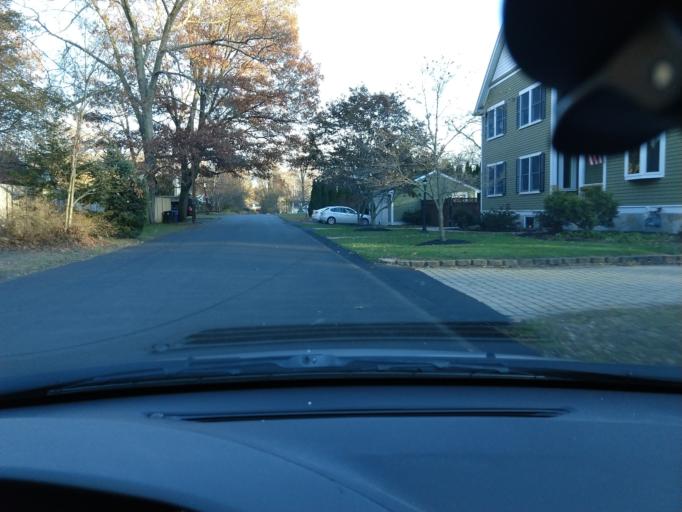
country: US
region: Massachusetts
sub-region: Middlesex County
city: Bedford
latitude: 42.4876
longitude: -71.2724
